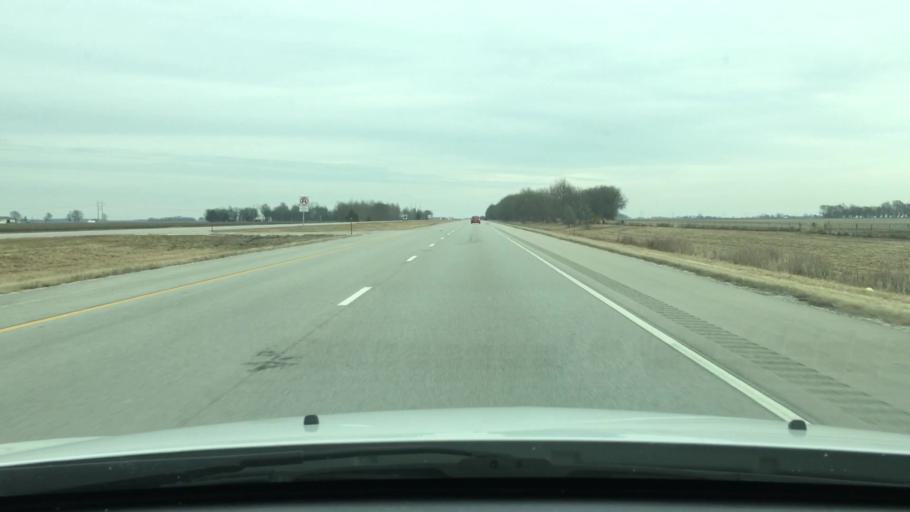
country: US
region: Illinois
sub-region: Sangamon County
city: New Berlin
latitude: 39.7368
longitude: -90.0283
